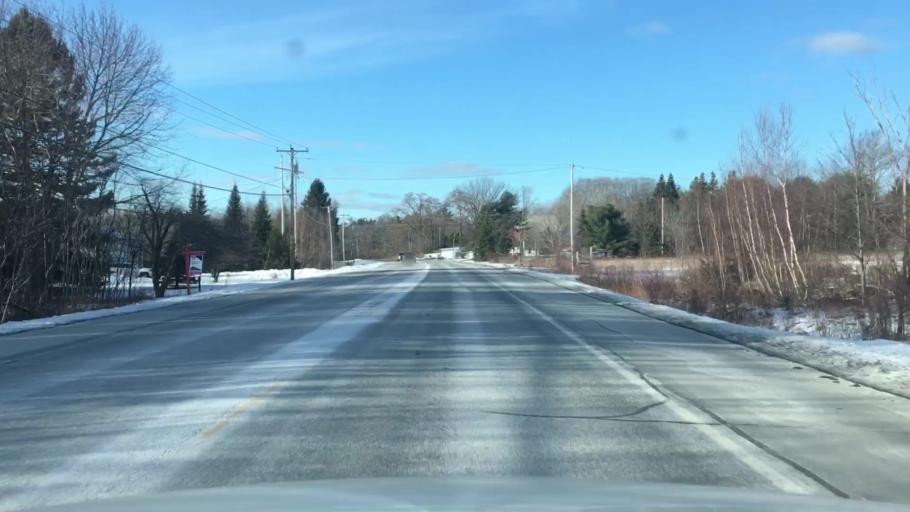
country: US
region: Maine
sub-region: Penobscot County
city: Holden
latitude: 44.8005
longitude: -68.5970
